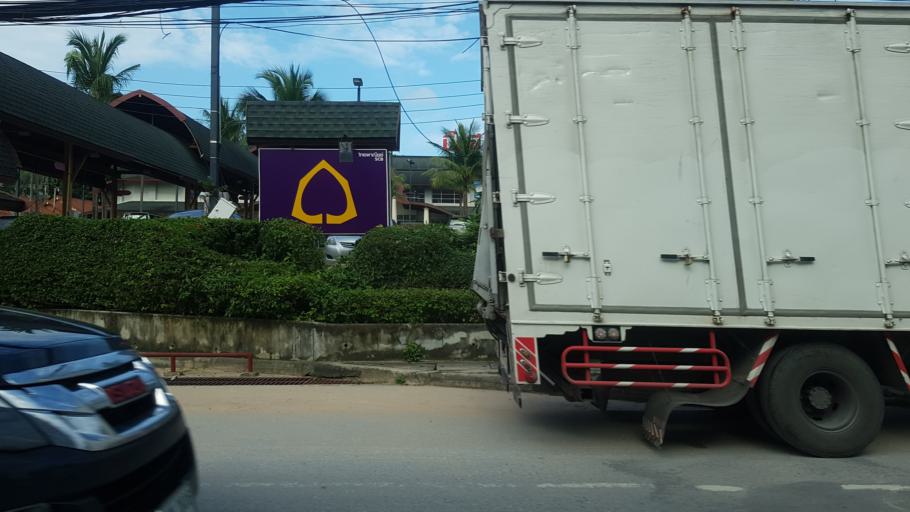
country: TH
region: Surat Thani
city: Ko Samui
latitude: 9.5452
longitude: 100.0392
